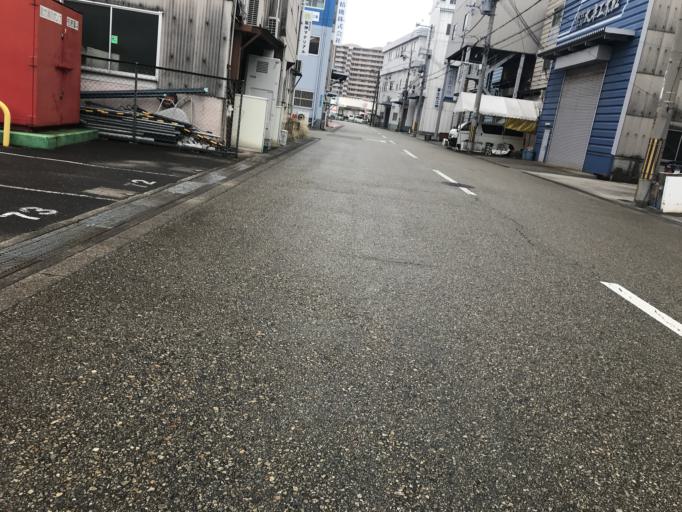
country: JP
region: Osaka
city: Sakai
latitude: 34.6253
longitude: 135.4714
